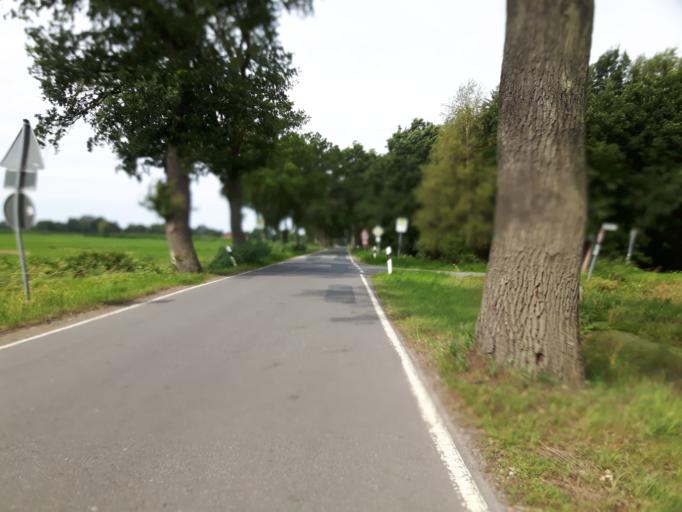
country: DE
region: Lower Saxony
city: Rastede
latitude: 53.2839
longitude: 8.2931
